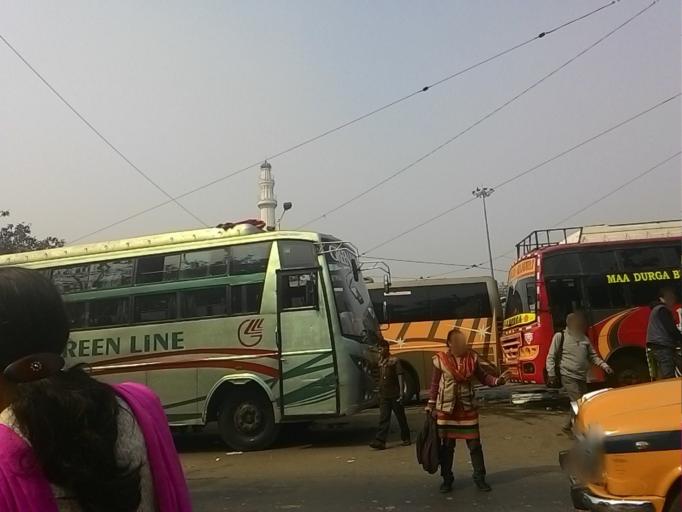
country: IN
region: West Bengal
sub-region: Kolkata
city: Bara Bazar
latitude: 22.5626
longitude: 88.3505
